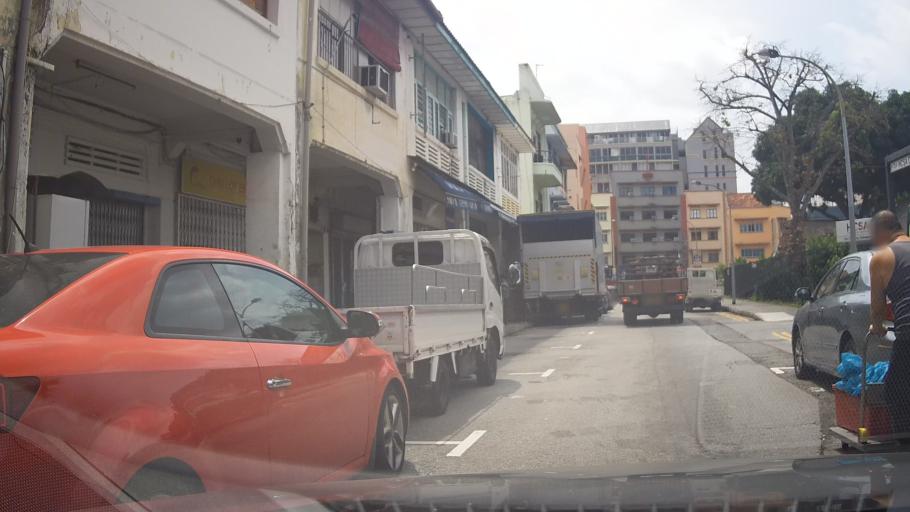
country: SG
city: Singapore
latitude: 1.3139
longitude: 103.8814
